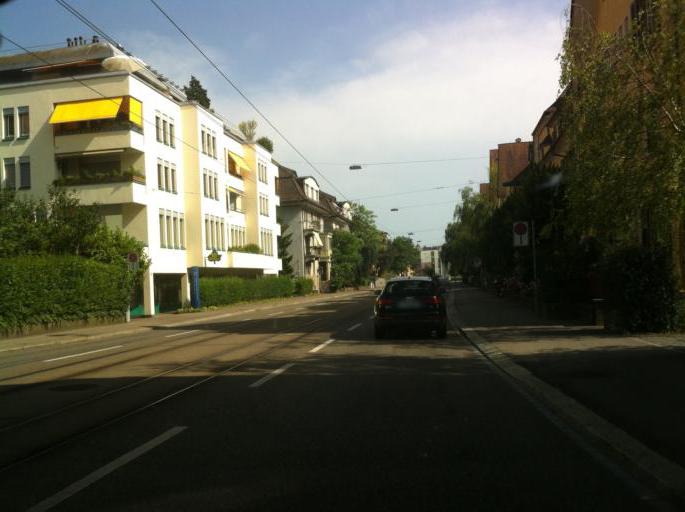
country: CH
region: Zurich
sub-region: Bezirk Zuerich
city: Zuerich (Kreis 6) / Oberstrass
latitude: 47.3887
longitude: 8.5464
